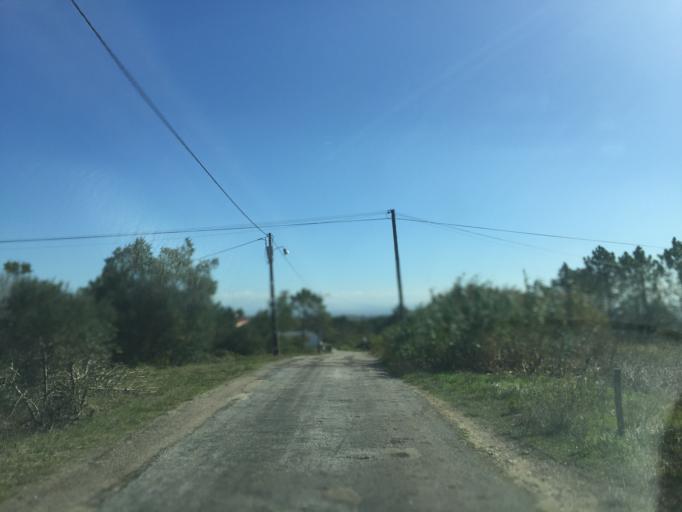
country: PT
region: Coimbra
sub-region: Figueira da Foz
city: Tavarede
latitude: 40.1911
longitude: -8.8373
